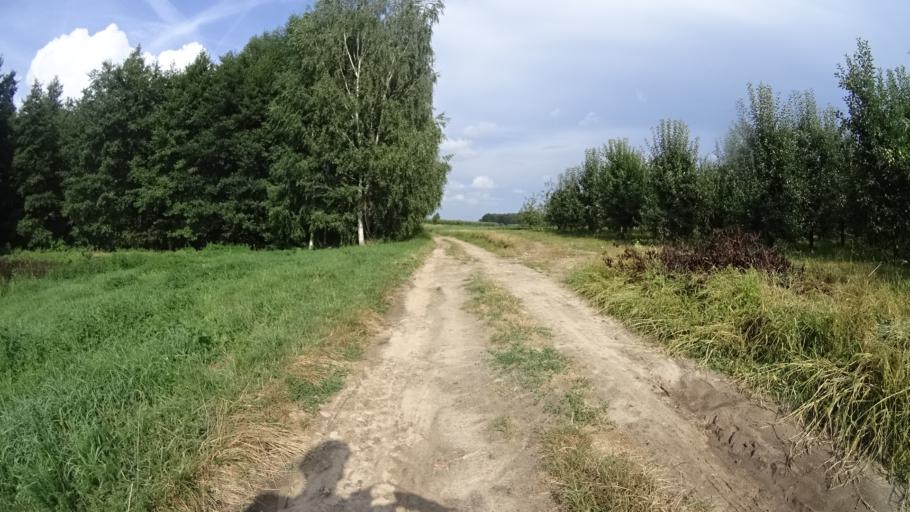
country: PL
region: Masovian Voivodeship
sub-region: Powiat grojecki
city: Goszczyn
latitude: 51.6998
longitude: 20.8506
